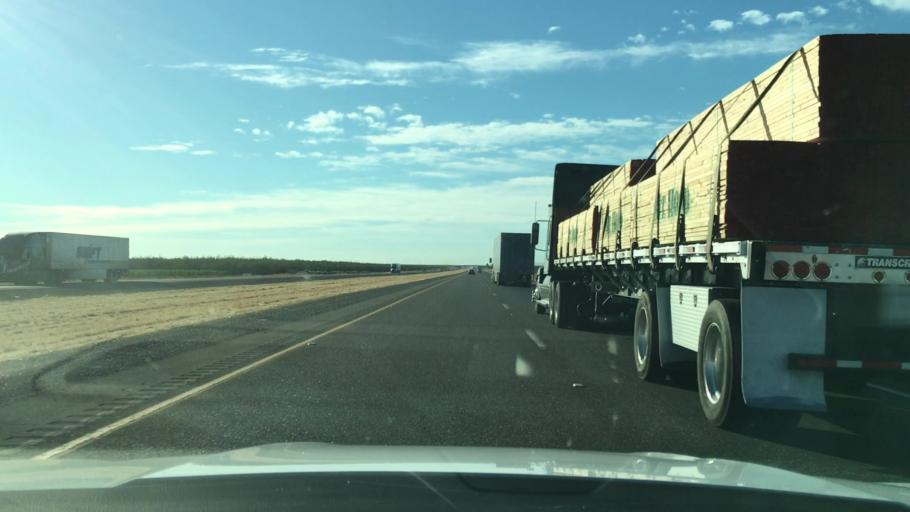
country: US
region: California
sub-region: Merced County
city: South Dos Palos
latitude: 36.8016
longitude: -120.7407
